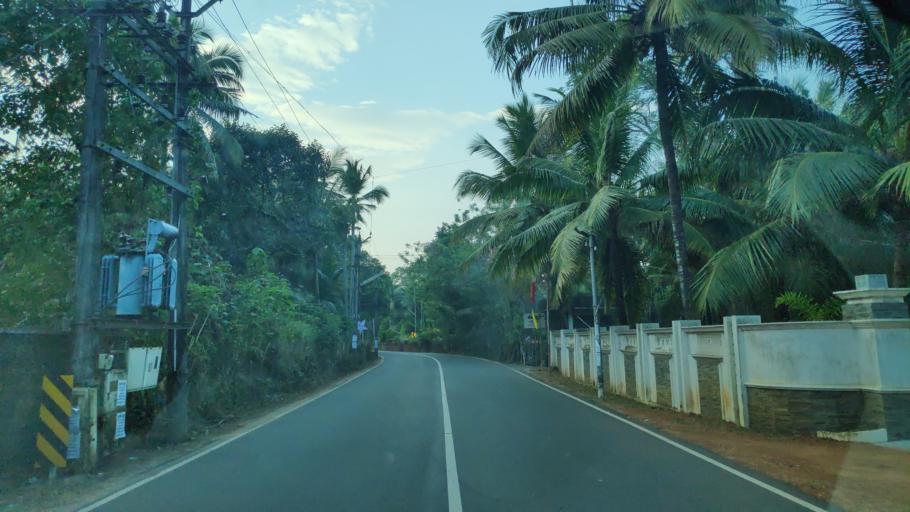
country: IN
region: Kerala
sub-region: Alappuzha
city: Shertallai
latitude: 9.6805
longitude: 76.3714
